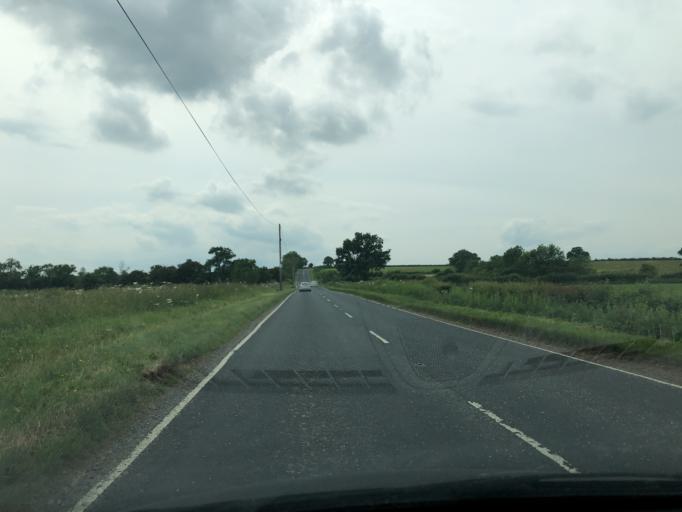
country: GB
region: England
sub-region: North Yorkshire
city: Pickering
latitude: 54.2612
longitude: -0.8348
